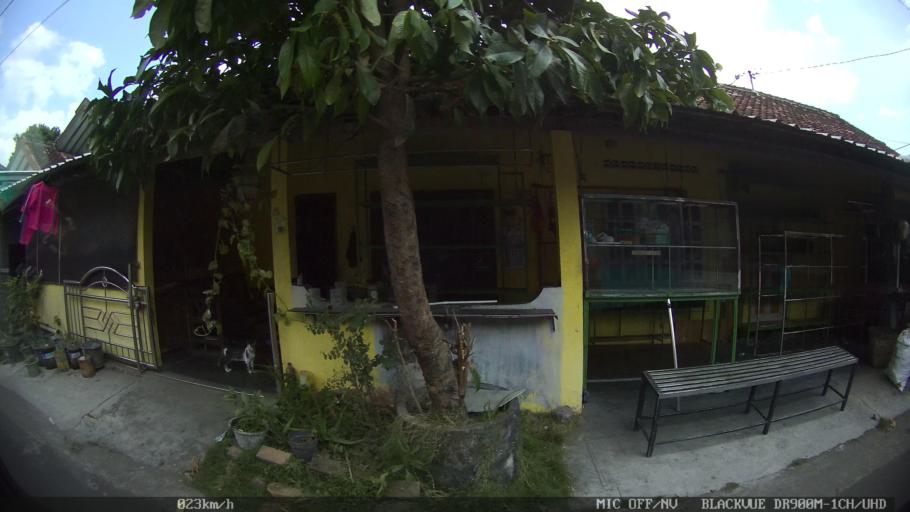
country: ID
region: Daerah Istimewa Yogyakarta
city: Kasihan
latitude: -7.8138
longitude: 110.3438
